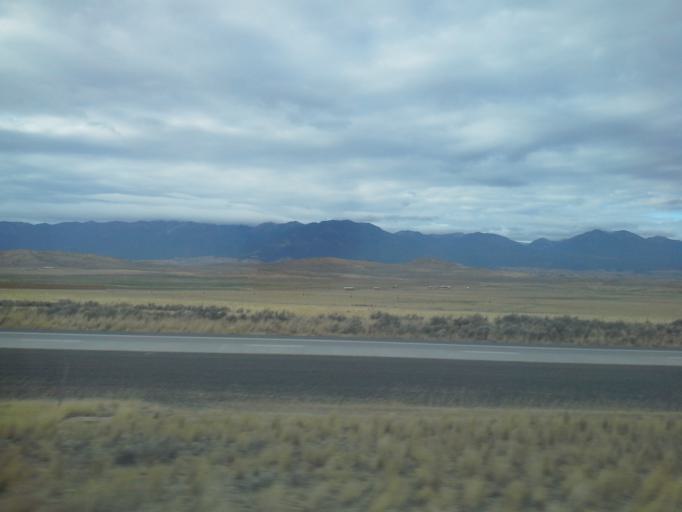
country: US
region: Oregon
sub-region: Baker County
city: Baker City
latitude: 44.9383
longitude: -117.8414
